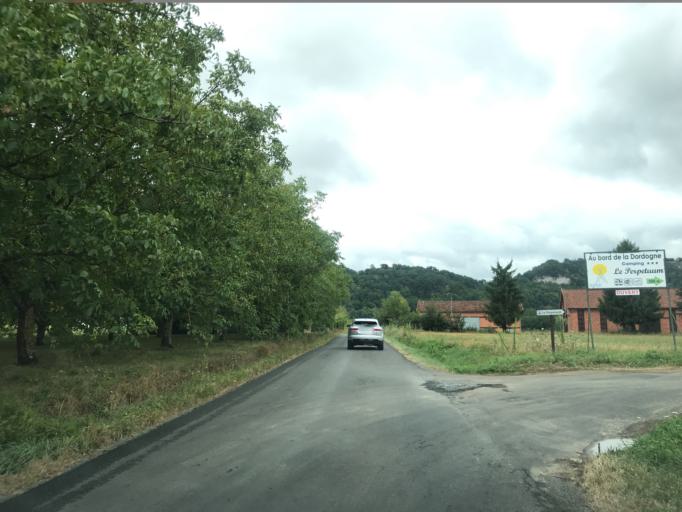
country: FR
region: Aquitaine
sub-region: Departement de la Dordogne
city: Domme
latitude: 44.8142
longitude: 1.2241
